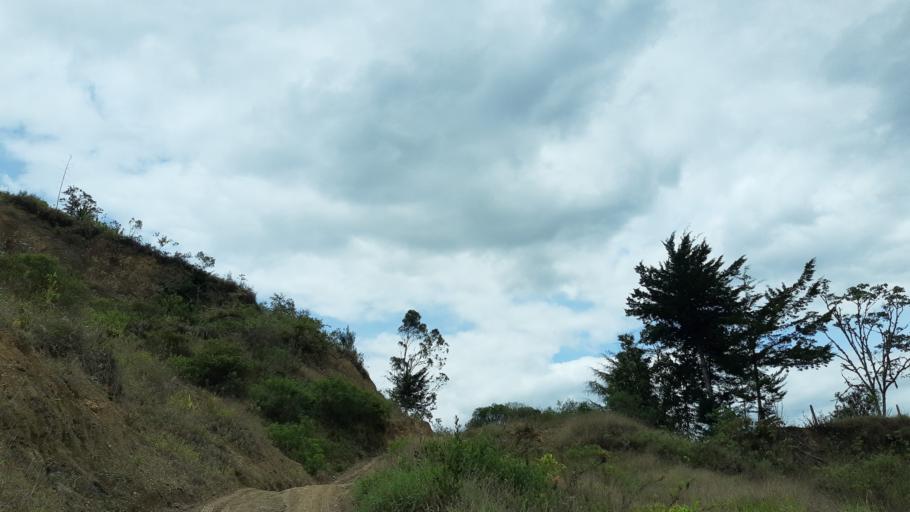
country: CO
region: Boyaca
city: Garagoa
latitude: 5.0647
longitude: -73.3620
